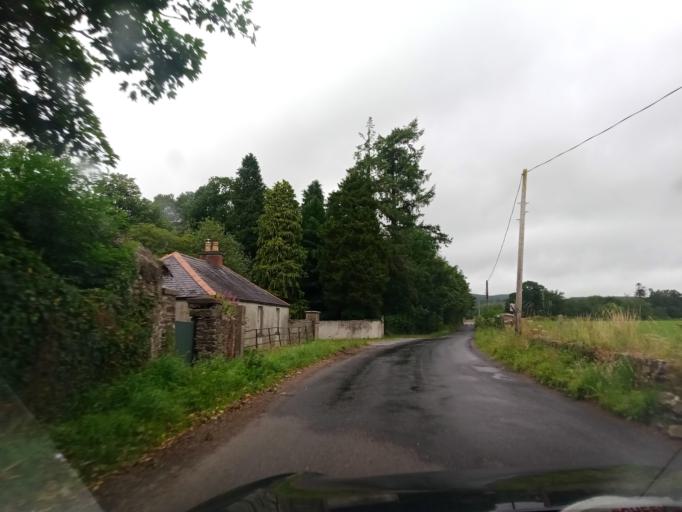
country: IE
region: Leinster
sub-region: Laois
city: Abbeyleix
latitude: 52.9268
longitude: -7.2813
